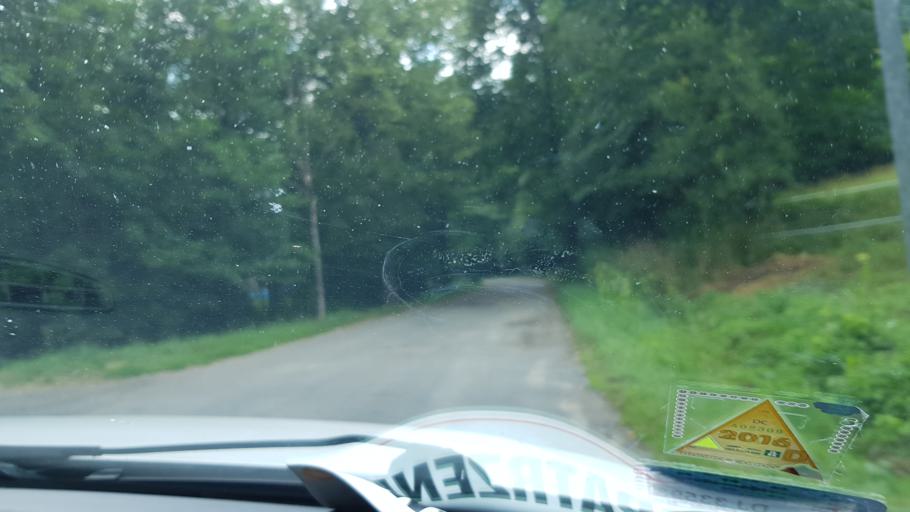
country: PL
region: Lower Silesian Voivodeship
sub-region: Powiat jeleniogorski
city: Jezow Sudecki
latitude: 50.9726
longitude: 15.8045
